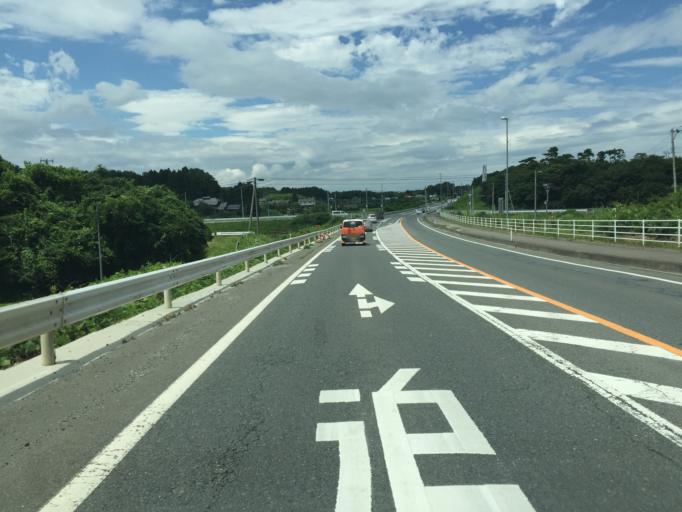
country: JP
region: Fukushima
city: Namie
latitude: 37.7258
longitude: 140.9534
